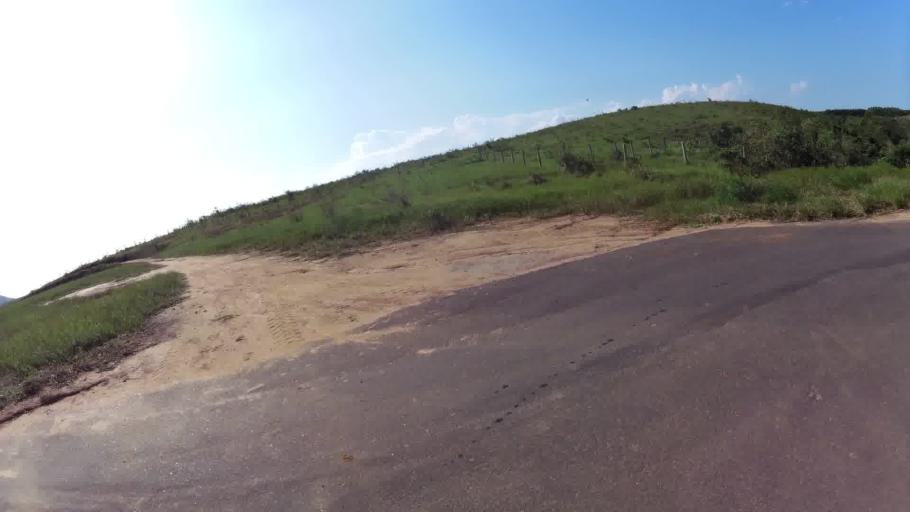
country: BR
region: Espirito Santo
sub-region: Guarapari
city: Guarapari
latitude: -20.7115
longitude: -40.5374
